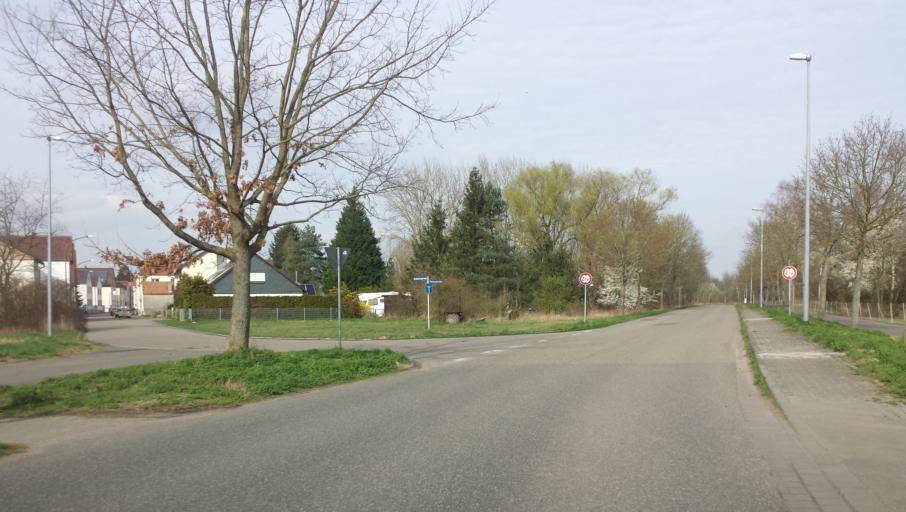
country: DE
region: Rheinland-Pfalz
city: Schifferstadt
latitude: 49.3767
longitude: 8.3673
